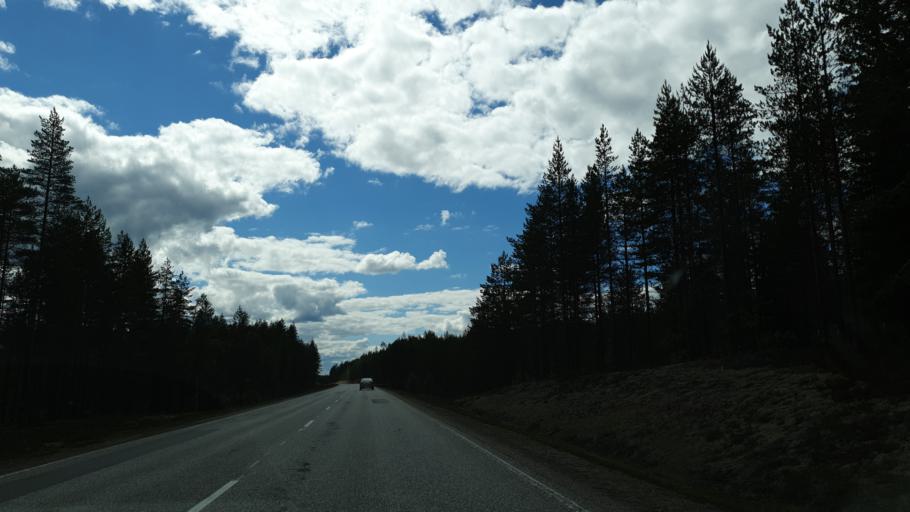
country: FI
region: North Karelia
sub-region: Pielisen Karjala
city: Valtimo
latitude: 63.4668
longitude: 28.8070
